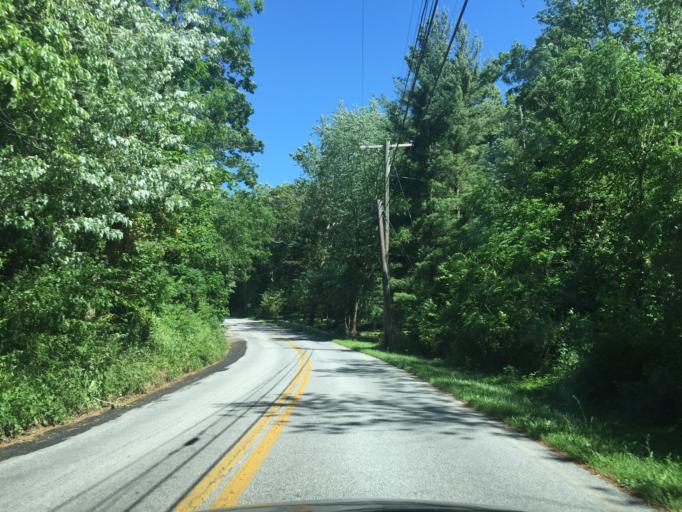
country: US
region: Maryland
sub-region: Carroll County
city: Hampstead
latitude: 39.6166
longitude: -76.8915
